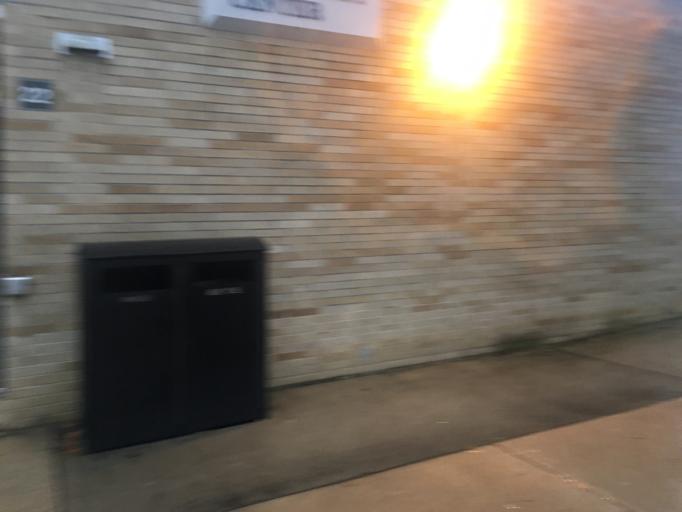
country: US
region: Wisconsin
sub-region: Walworth County
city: Whitewater
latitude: 42.8375
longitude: -88.7437
